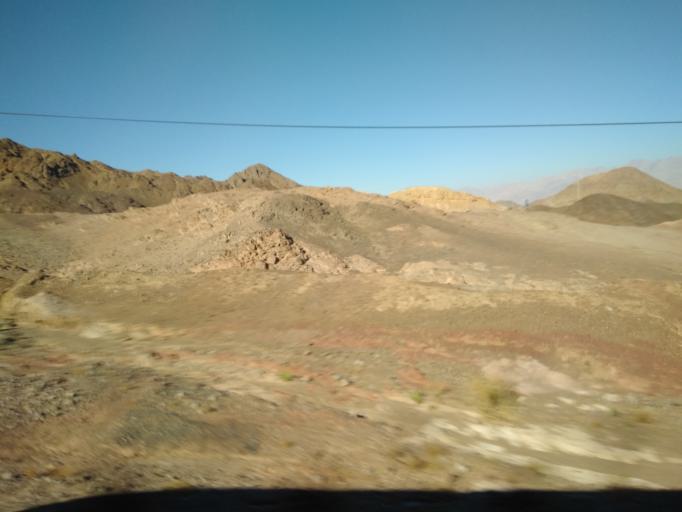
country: IL
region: Southern District
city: Eilat
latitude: 29.5560
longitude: 34.9095
